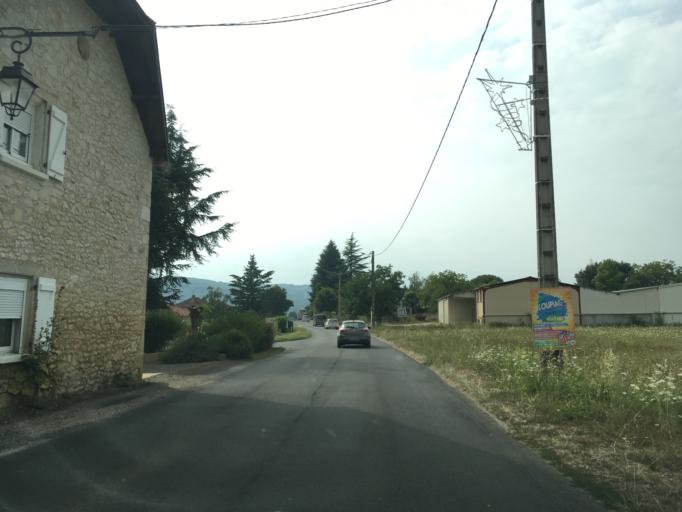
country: FR
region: Midi-Pyrenees
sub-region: Departement du Lot
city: Souillac
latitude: 44.8560
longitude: 1.5107
